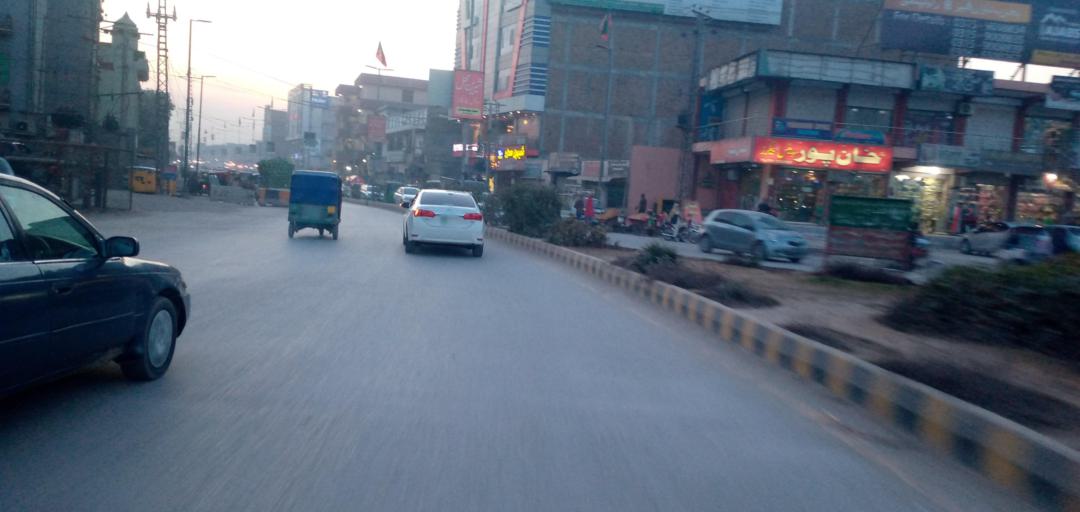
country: PK
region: Khyber Pakhtunkhwa
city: Peshawar
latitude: 34.0318
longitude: 71.6065
